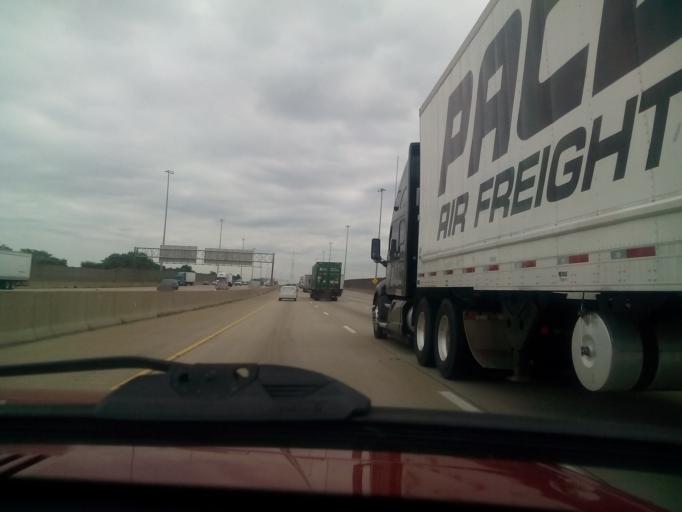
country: US
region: Illinois
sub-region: Cook County
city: Lansing
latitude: 41.5777
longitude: -87.5443
